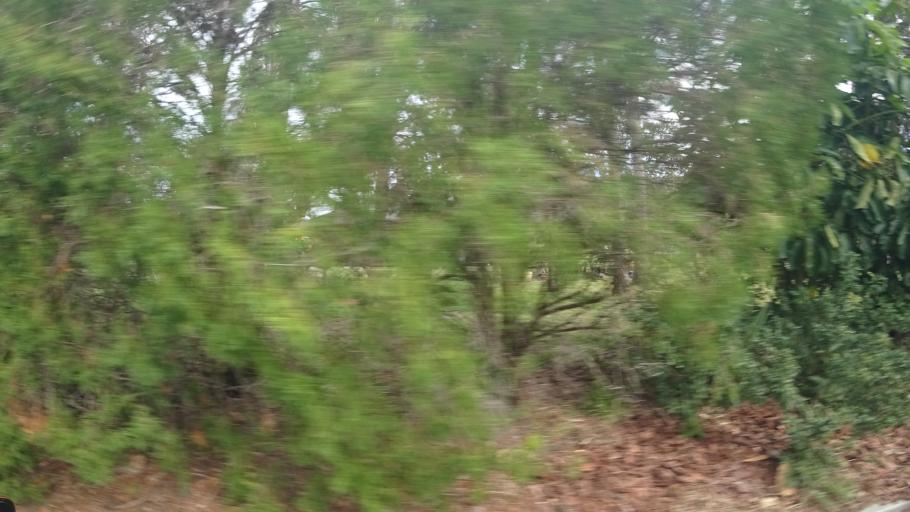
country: US
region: Florida
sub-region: Manatee County
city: West Bradenton
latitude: 27.4929
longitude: -82.6397
